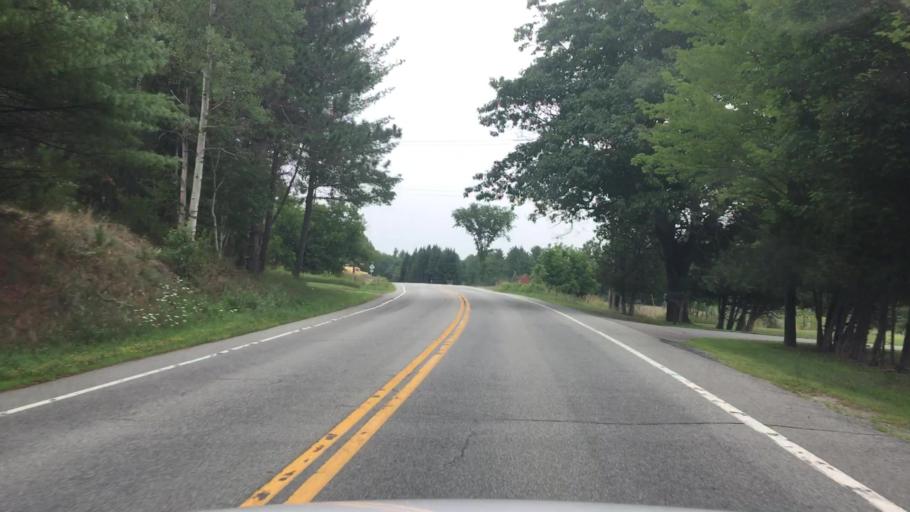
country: US
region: New York
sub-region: Essex County
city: Elizabethtown
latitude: 44.3886
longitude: -73.7106
